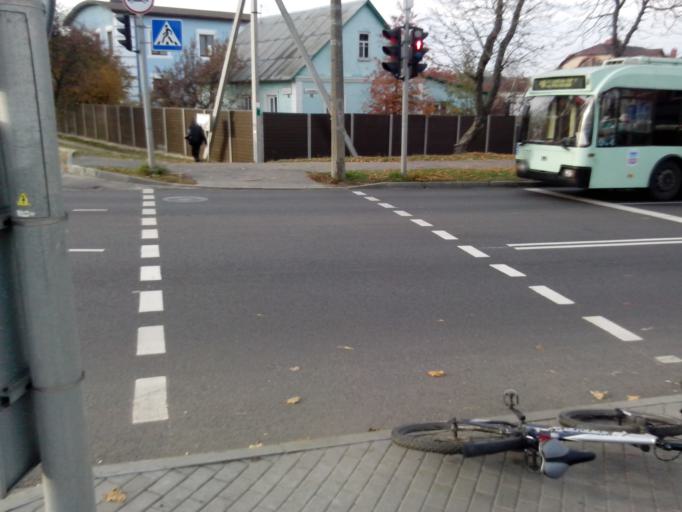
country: BY
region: Minsk
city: Minsk
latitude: 53.9491
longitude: 27.5969
